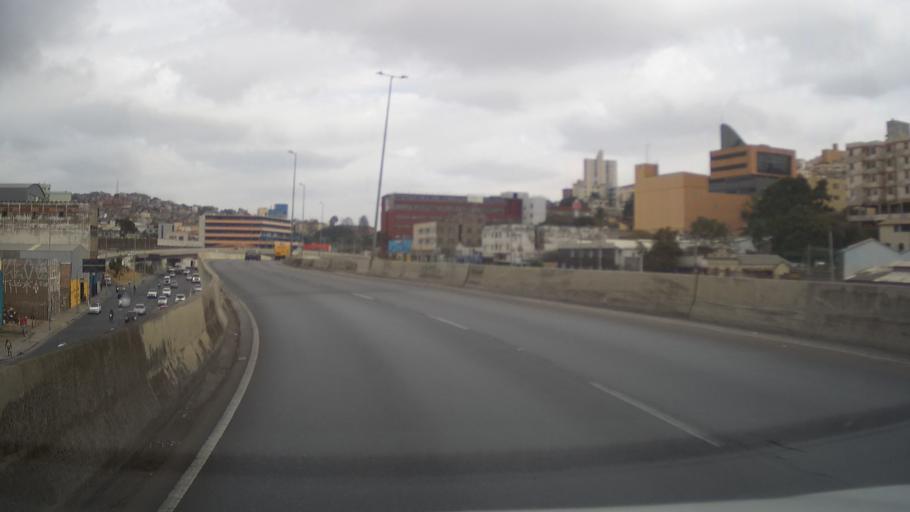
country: BR
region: Minas Gerais
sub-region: Belo Horizonte
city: Belo Horizonte
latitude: -19.9100
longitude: -43.9403
